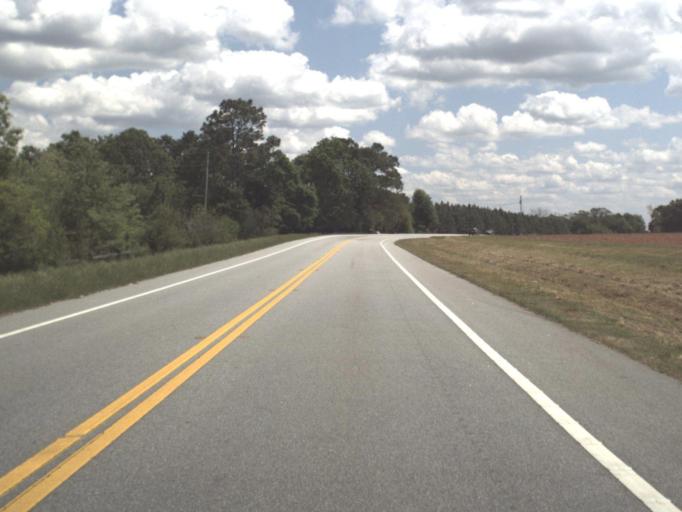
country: US
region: Alabama
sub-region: Escambia County
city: Atmore
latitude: 30.8825
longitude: -87.4482
